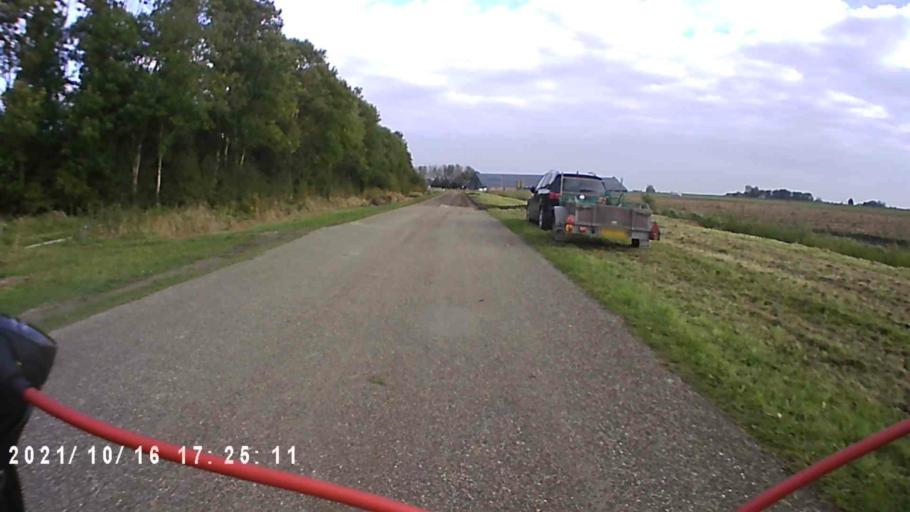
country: NL
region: Friesland
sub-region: Gemeente Kollumerland en Nieuwkruisland
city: Kollum
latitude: 53.3211
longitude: 6.1877
